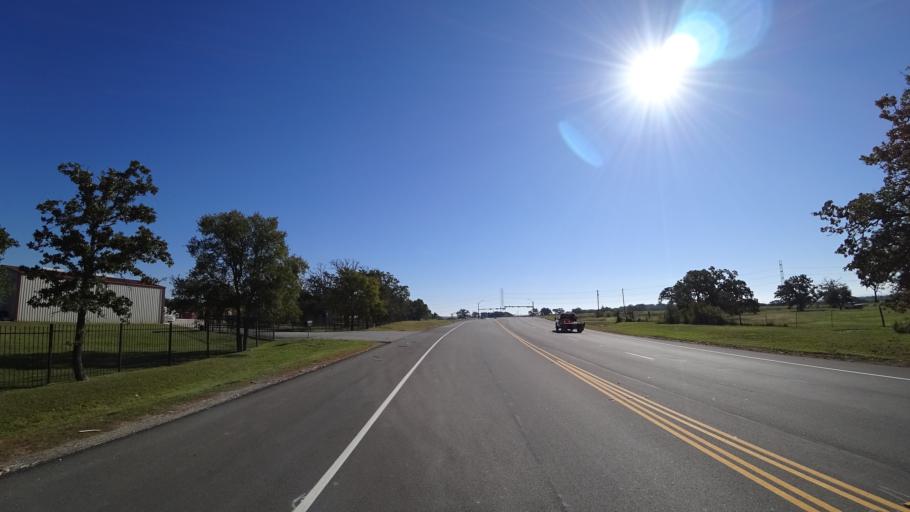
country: US
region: Texas
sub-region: Travis County
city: Hornsby Bend
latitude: 30.2885
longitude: -97.5787
